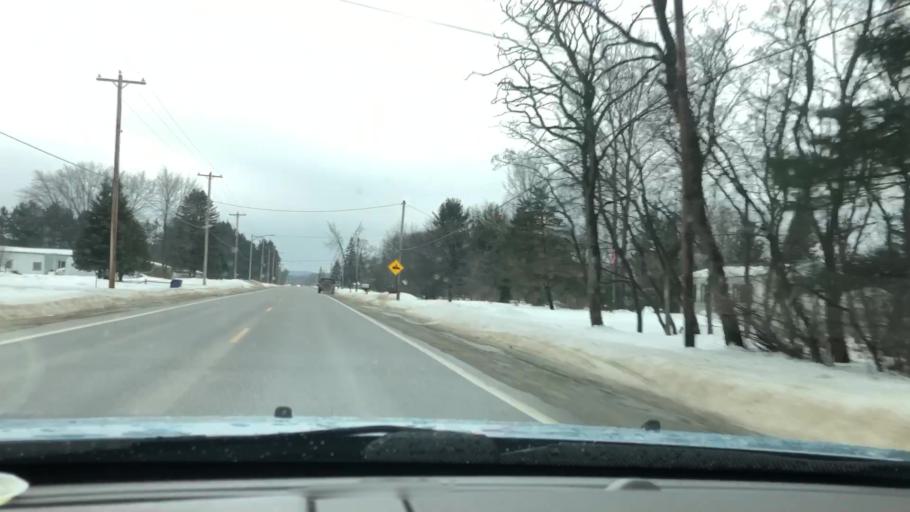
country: US
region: Michigan
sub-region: Charlevoix County
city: East Jordan
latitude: 45.1453
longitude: -85.1192
